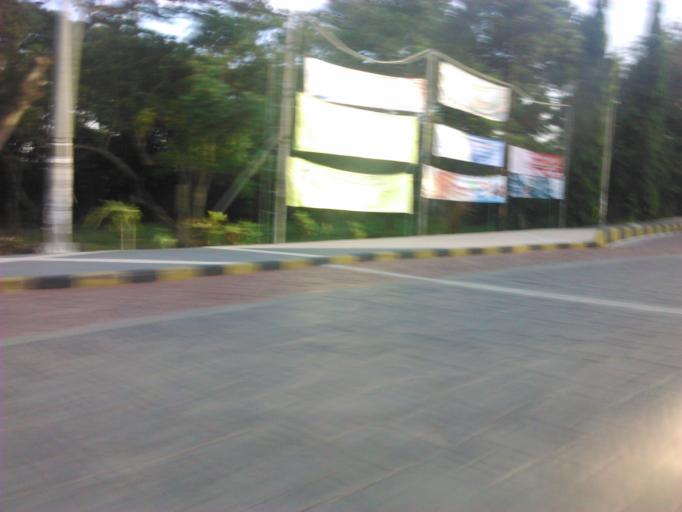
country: ID
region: East Java
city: Mulyorejo
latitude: -7.2795
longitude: 112.7906
